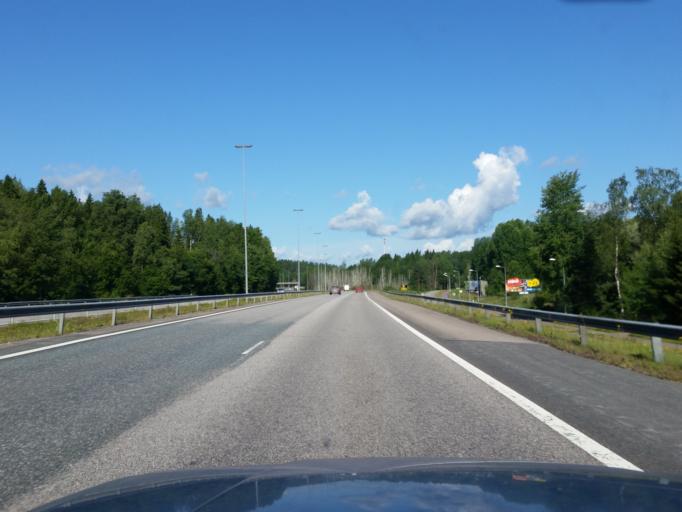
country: FI
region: Uusimaa
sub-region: Helsinki
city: Kirkkonummi
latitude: 60.2828
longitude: 24.4356
